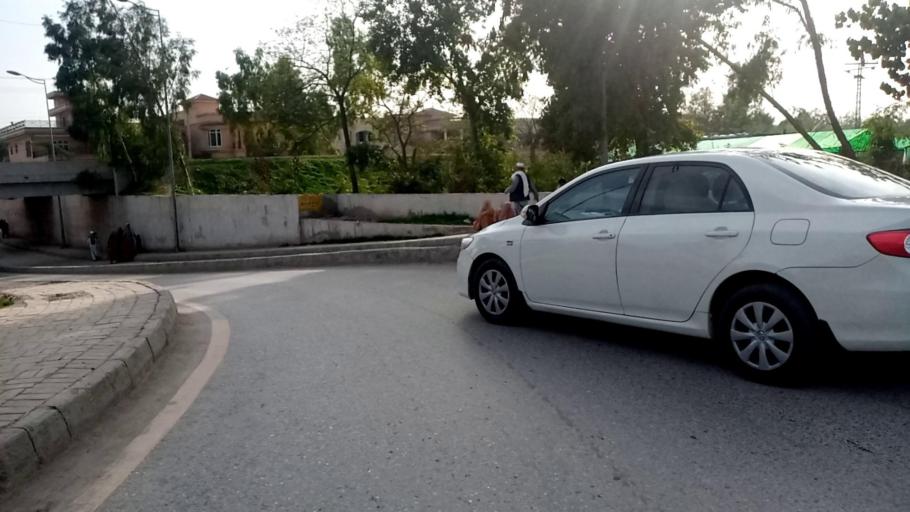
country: PK
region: Khyber Pakhtunkhwa
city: Peshawar
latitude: 33.9967
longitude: 71.4527
